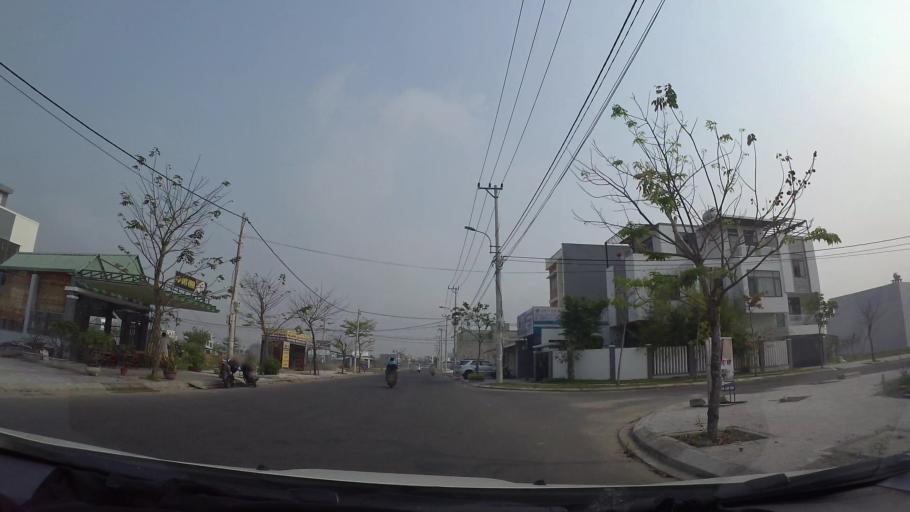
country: VN
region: Da Nang
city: Ngu Hanh Son
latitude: 16.0122
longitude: 108.2297
